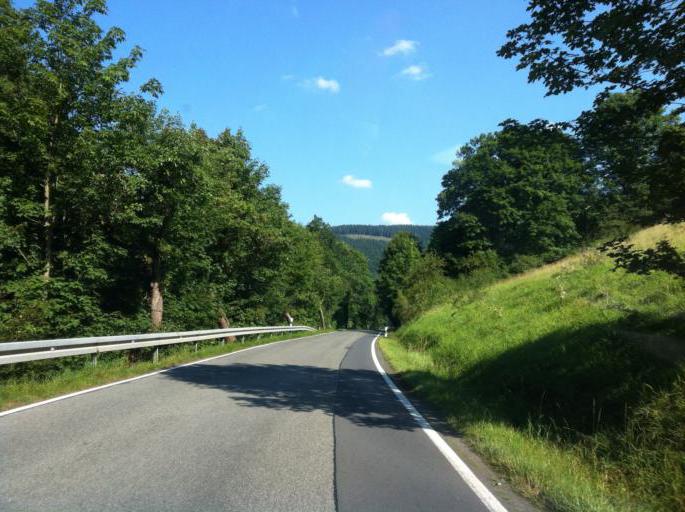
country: DE
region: Thuringia
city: Schalkau
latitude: 50.4173
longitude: 11.0395
